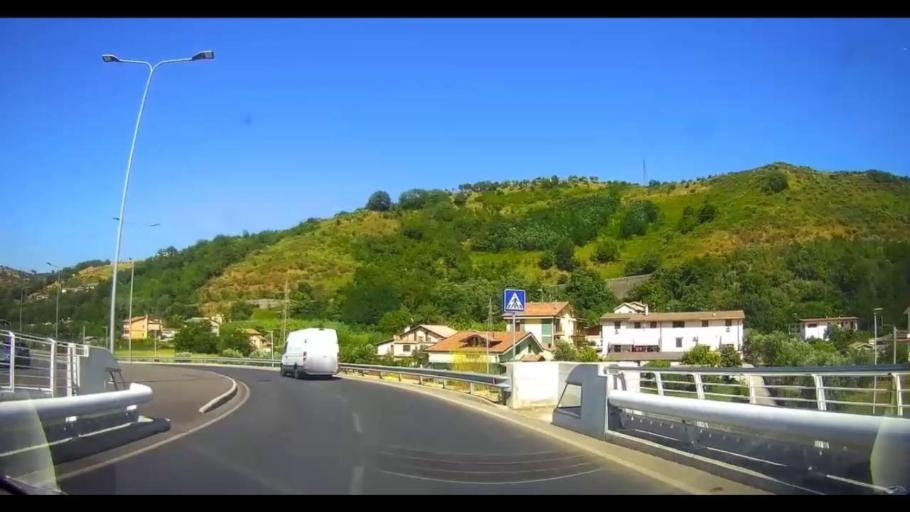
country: IT
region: Calabria
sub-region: Provincia di Cosenza
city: Cosenza
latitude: 39.2982
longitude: 16.2600
